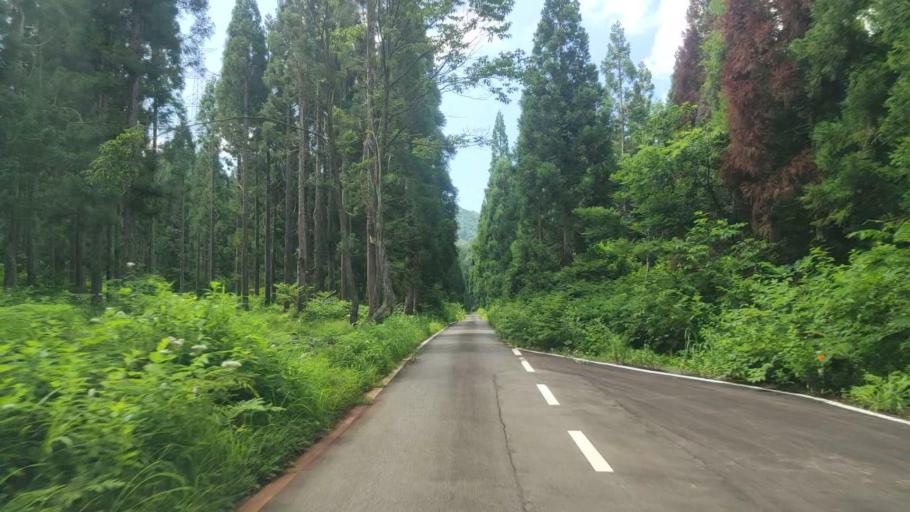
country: JP
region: Fukui
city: Katsuyama
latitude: 36.1691
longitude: 136.5239
